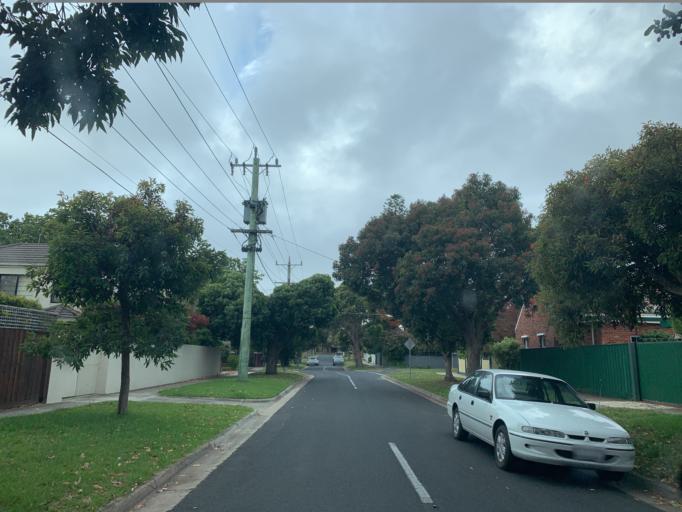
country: AU
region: Victoria
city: Hampton
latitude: -37.9501
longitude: 145.0166
